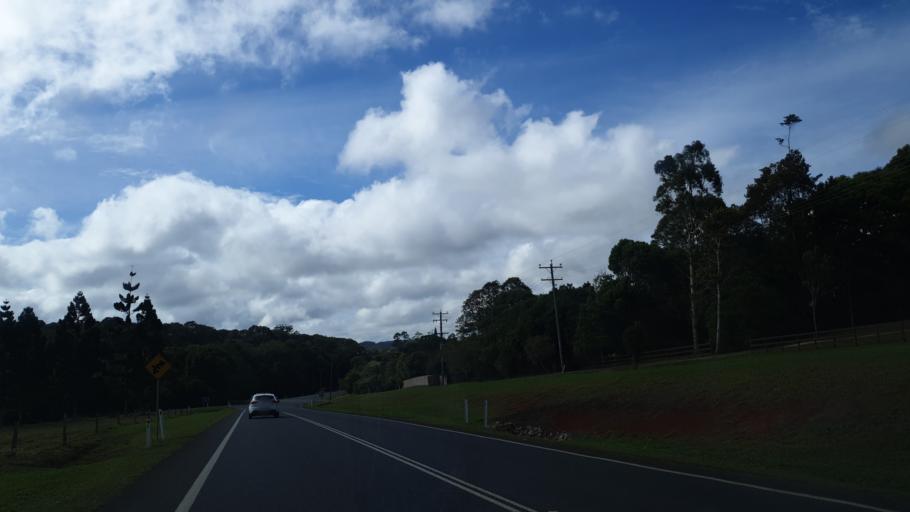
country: AU
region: Queensland
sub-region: Tablelands
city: Atherton
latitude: -17.3505
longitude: 145.5816
